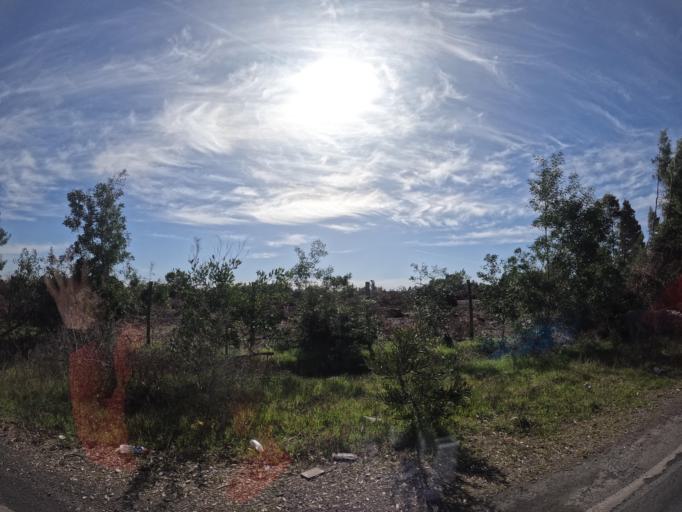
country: CL
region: Biobio
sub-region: Provincia de Biobio
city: Cabrero
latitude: -37.0394
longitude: -72.3739
